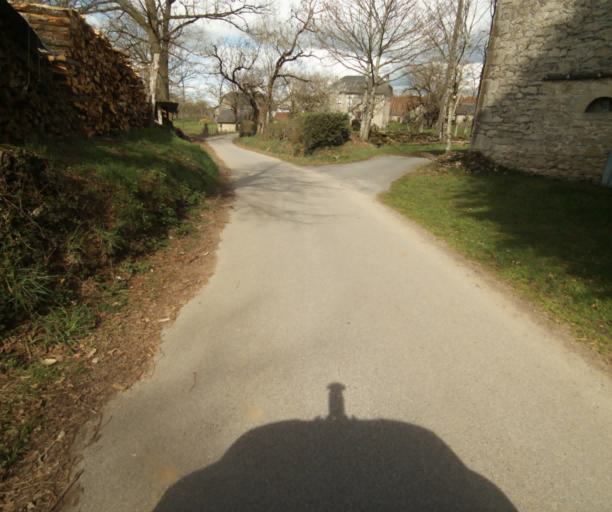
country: FR
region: Limousin
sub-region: Departement de la Correze
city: Correze
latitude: 45.3660
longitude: 1.8955
